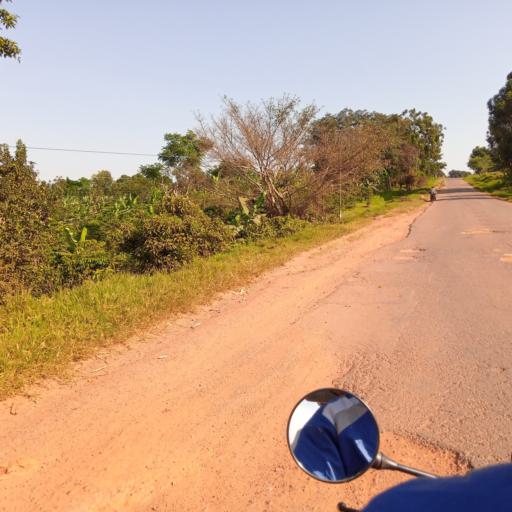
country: UG
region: Central Region
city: Masaka
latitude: -0.4404
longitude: 31.6643
